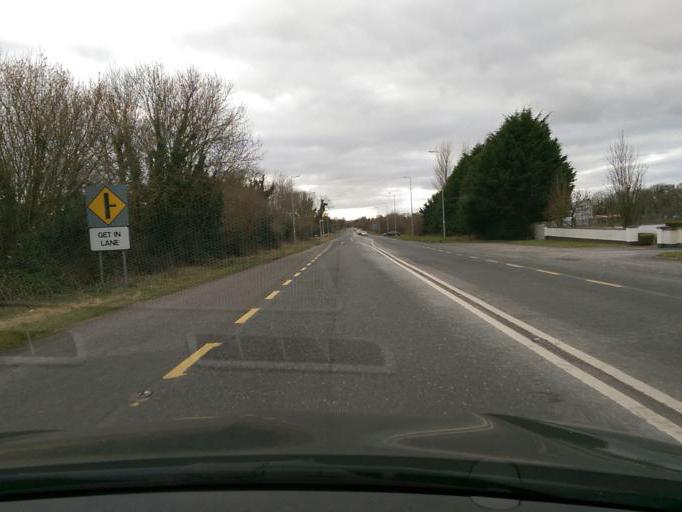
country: IE
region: Leinster
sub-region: An Iarmhi
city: Moate
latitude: 53.3898
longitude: -7.7802
